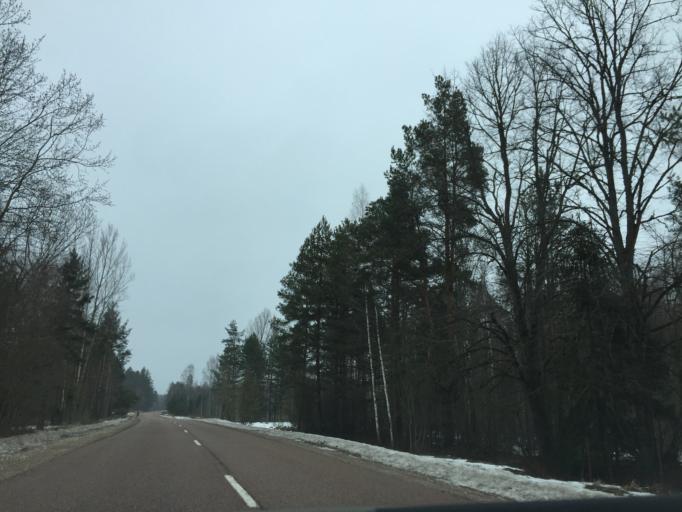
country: LV
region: Olaine
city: Olaine
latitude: 56.6332
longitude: 23.9347
